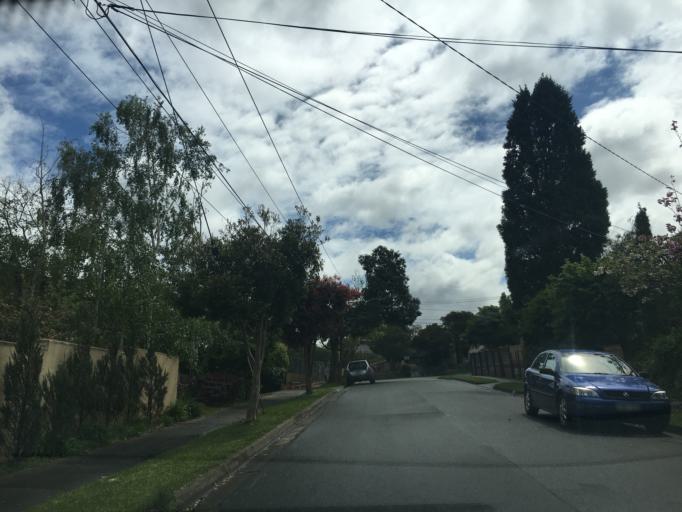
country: AU
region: Victoria
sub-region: Whitehorse
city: Vermont South
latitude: -37.8705
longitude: 145.1649
